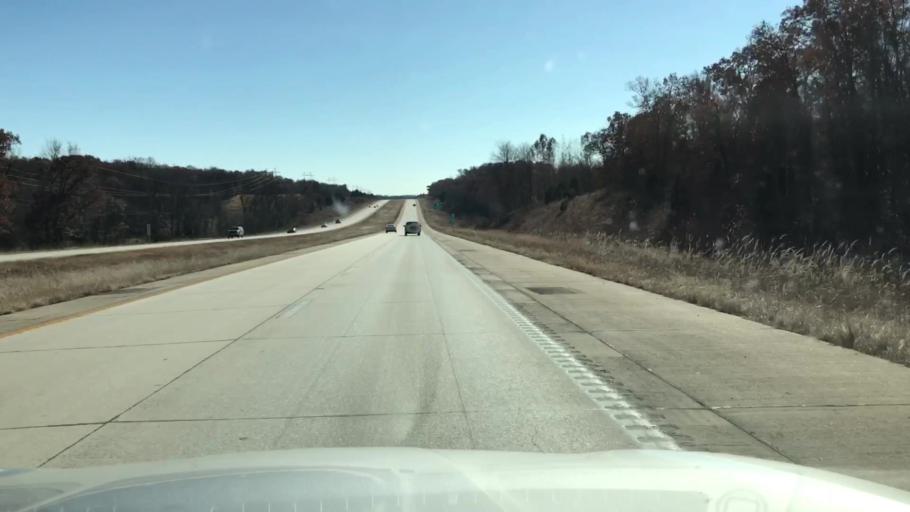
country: US
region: Missouri
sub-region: Jasper County
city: Duquesne
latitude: 37.0185
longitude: -94.4304
